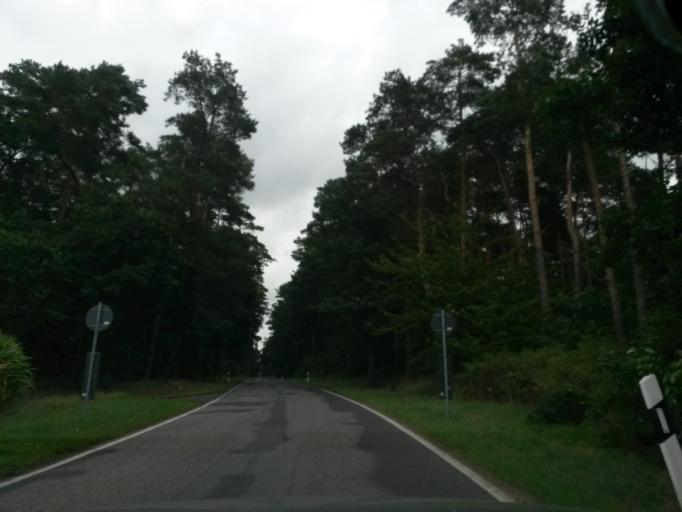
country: DE
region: Brandenburg
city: Angermunde
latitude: 53.0947
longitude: 13.9065
